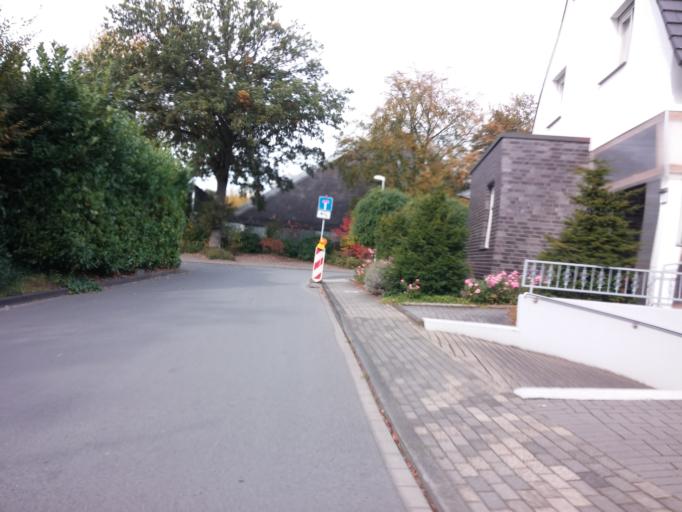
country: DE
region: North Rhine-Westphalia
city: Dorsten
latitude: 51.6338
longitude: 7.0120
